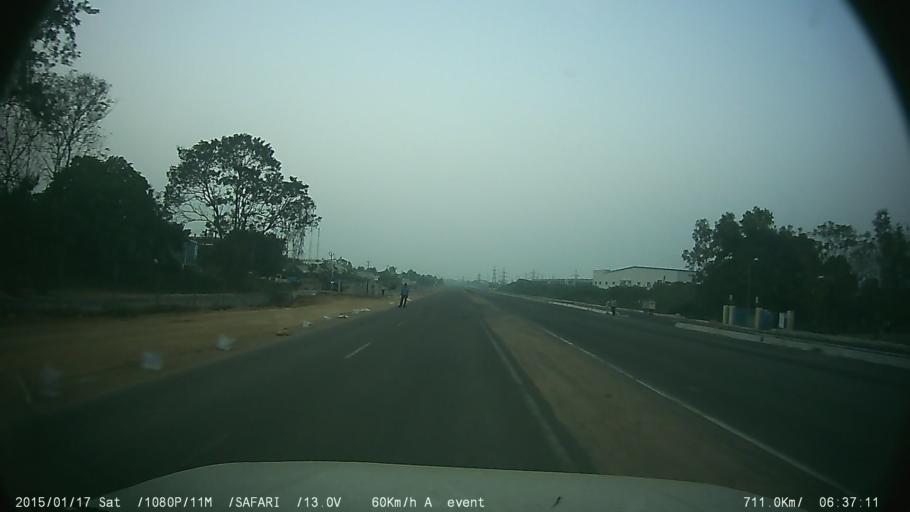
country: IN
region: Tamil Nadu
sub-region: Kancheepuram
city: Sriperumbudur
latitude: 12.9490
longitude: 79.9384
